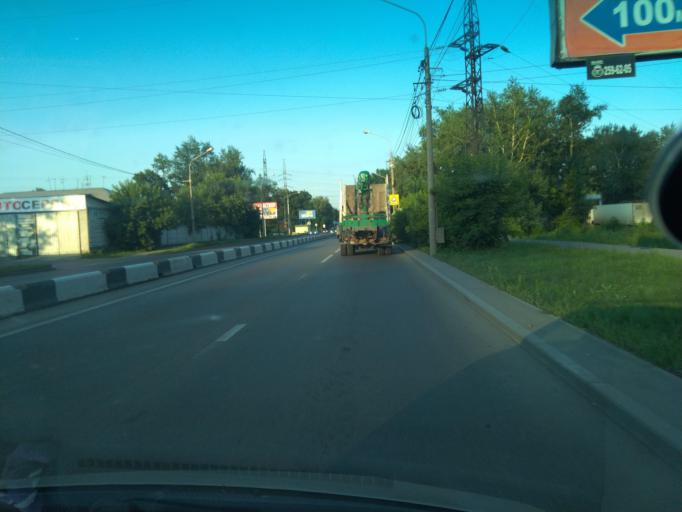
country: RU
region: Krasnoyarskiy
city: Berezovka
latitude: 56.0214
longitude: 93.0438
